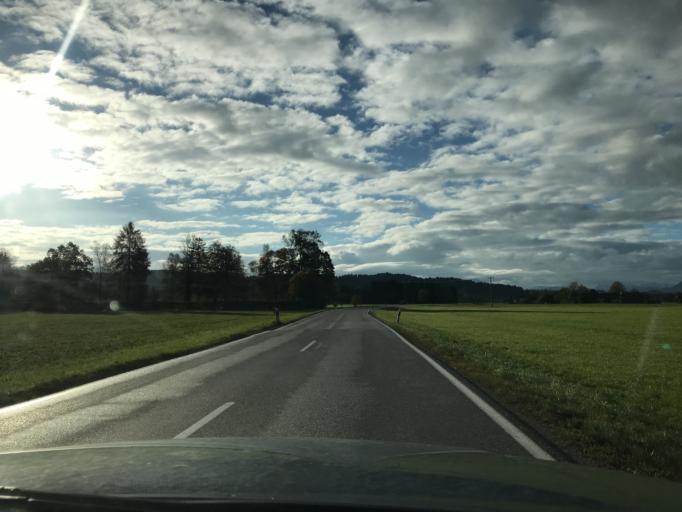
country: DE
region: Bavaria
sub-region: Upper Bavaria
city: Geretsried
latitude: 47.8400
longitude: 11.5280
